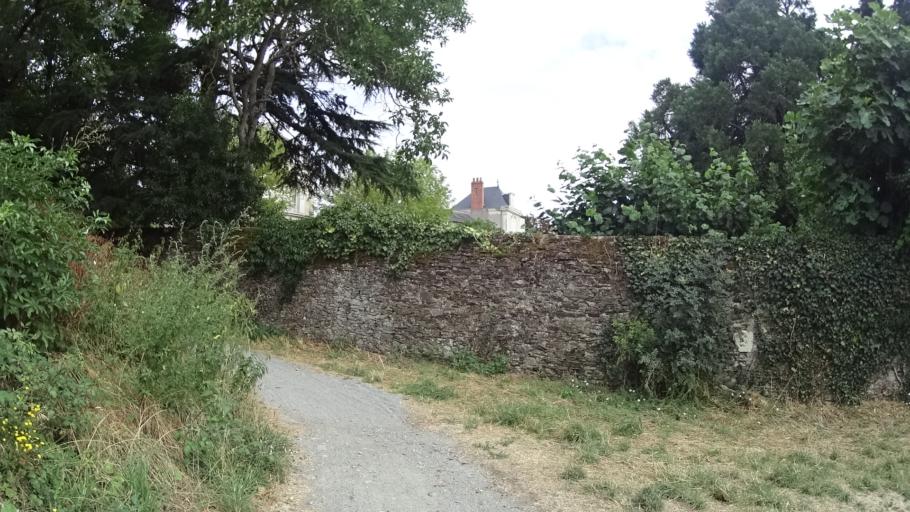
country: FR
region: Pays de la Loire
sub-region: Departement de Maine-et-Loire
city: Bouchemaine
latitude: 47.4044
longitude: -0.6226
